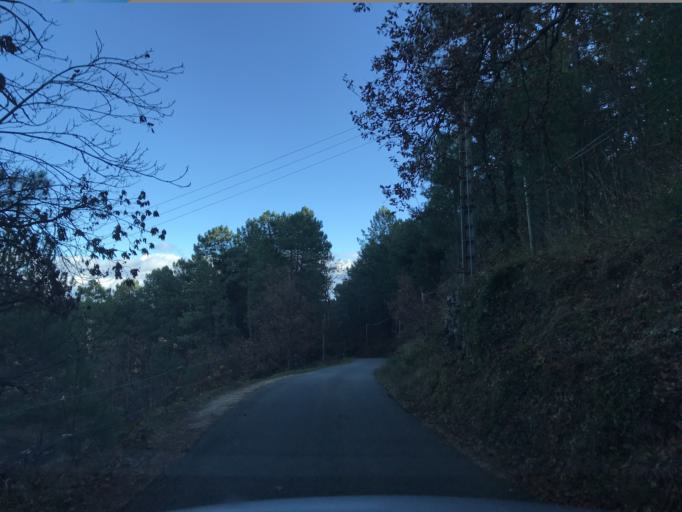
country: FR
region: Rhone-Alpes
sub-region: Departement de l'Ardeche
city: Les Vans
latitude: 44.4243
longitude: 4.0830
